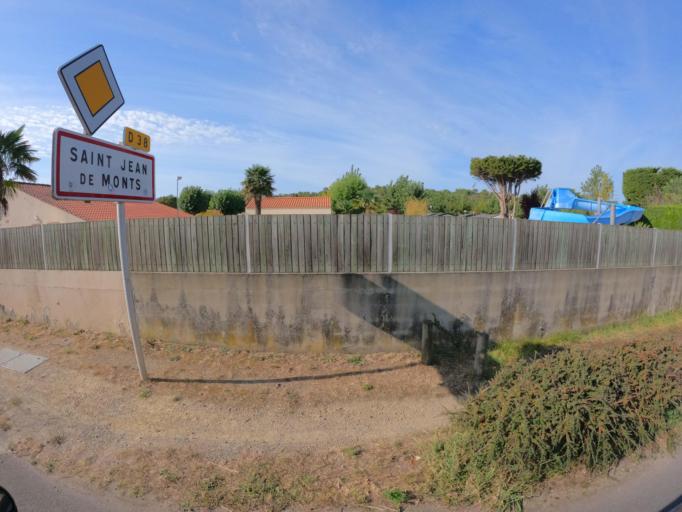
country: FR
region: Pays de la Loire
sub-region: Departement de la Vendee
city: Saint-Jean-de-Monts
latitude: 46.8009
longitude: -2.0807
